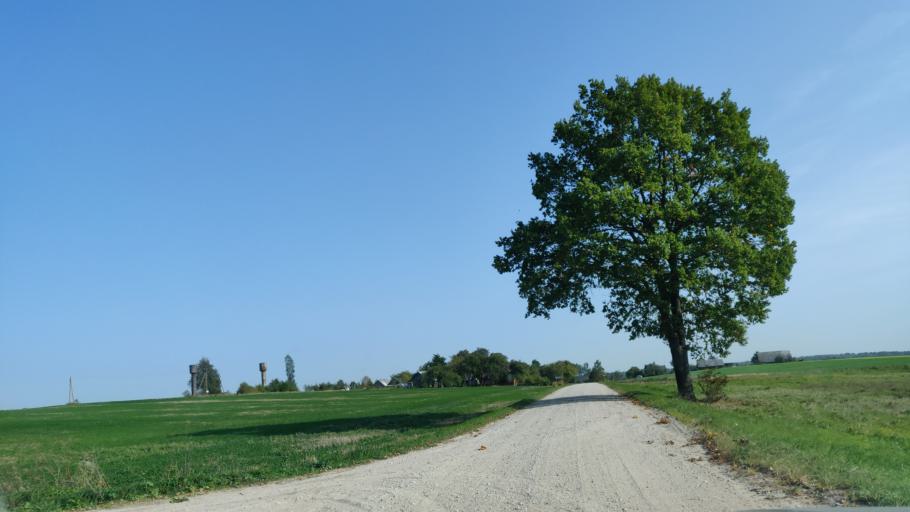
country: LT
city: Sirvintos
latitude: 54.9716
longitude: 24.8282
